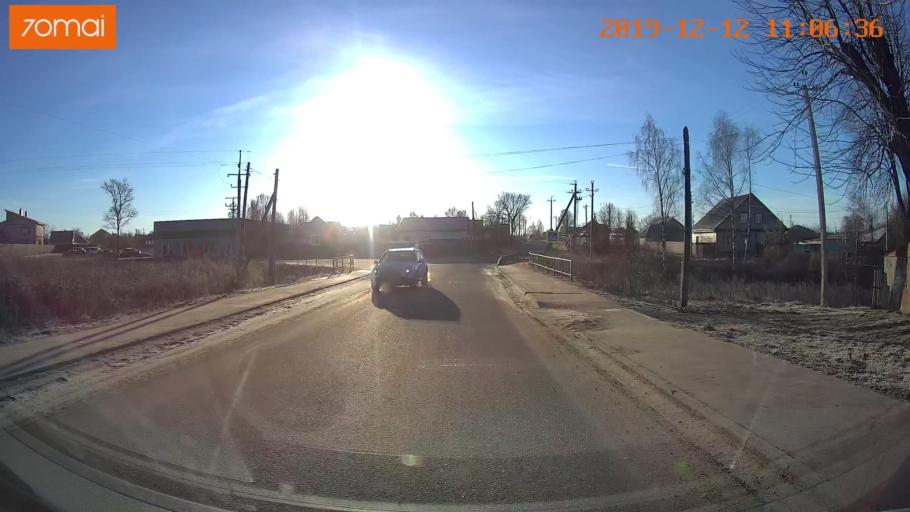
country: RU
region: Ivanovo
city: Kokhma
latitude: 56.9428
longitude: 41.0885
